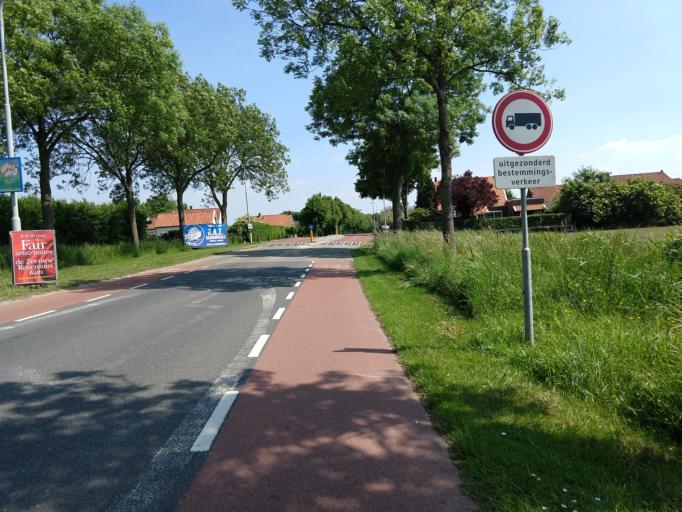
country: NL
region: Zeeland
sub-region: Gemeente Borsele
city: Borssele
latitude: 51.4325
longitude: 3.8155
